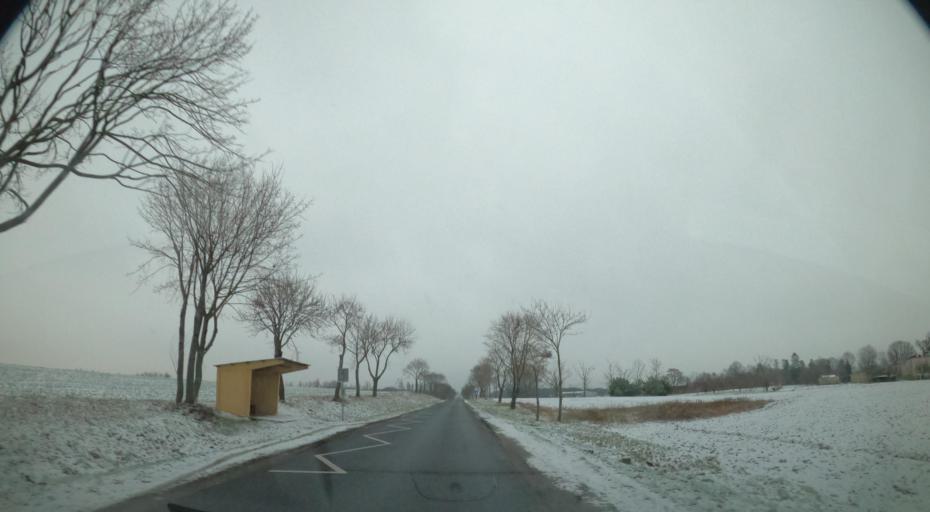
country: PL
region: Kujawsko-Pomorskie
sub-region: Powiat lipnowski
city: Wielgie
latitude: 52.6973
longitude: 19.2814
